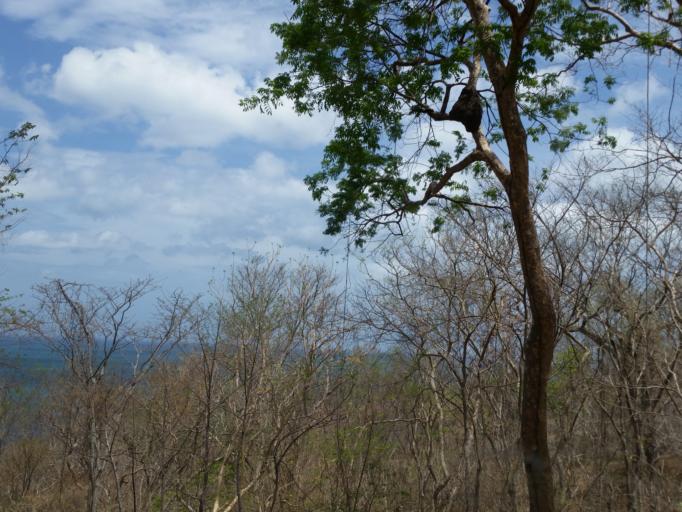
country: NI
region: Rivas
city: Tola
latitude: 11.4226
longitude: -86.0697
